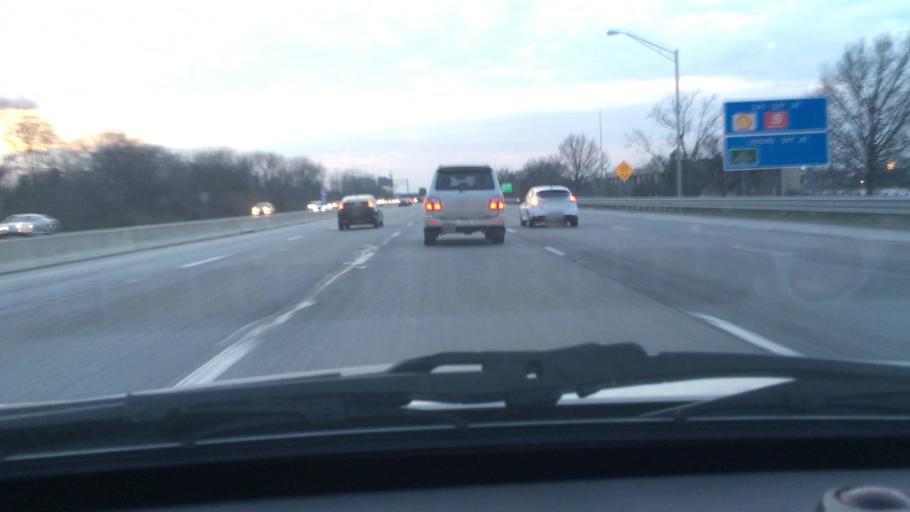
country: US
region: Indiana
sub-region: Marion County
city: Lawrence
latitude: 39.8998
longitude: -86.0615
